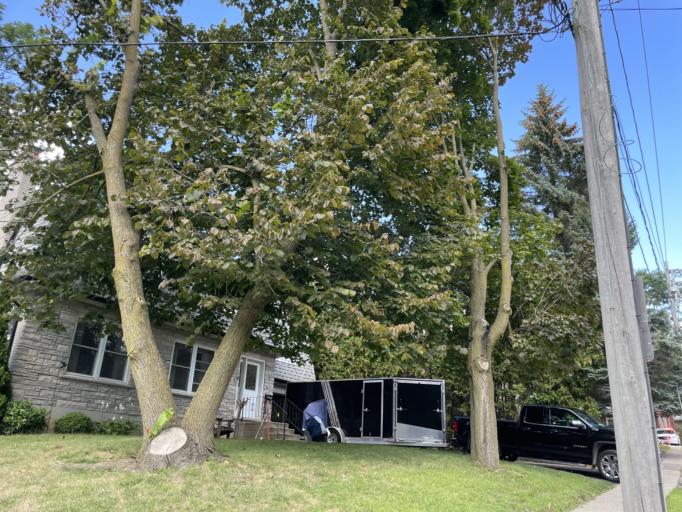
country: CA
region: Ontario
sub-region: Wellington County
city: Guelph
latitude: 43.5536
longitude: -80.2516
